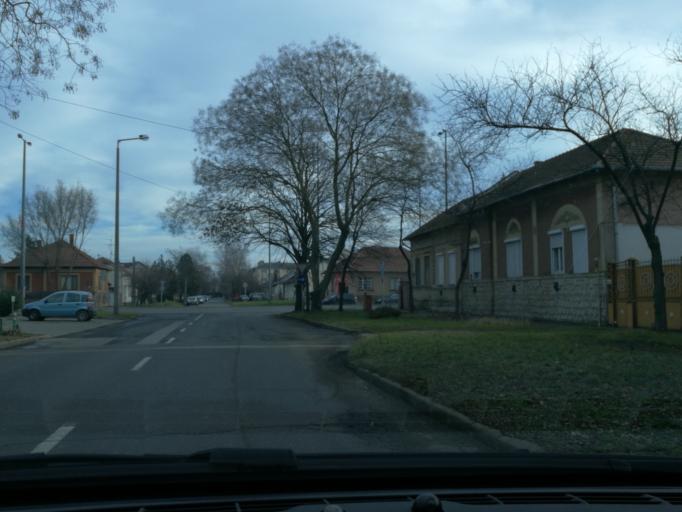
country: HU
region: Szabolcs-Szatmar-Bereg
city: Nyiregyhaza
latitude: 47.9547
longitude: 21.7269
